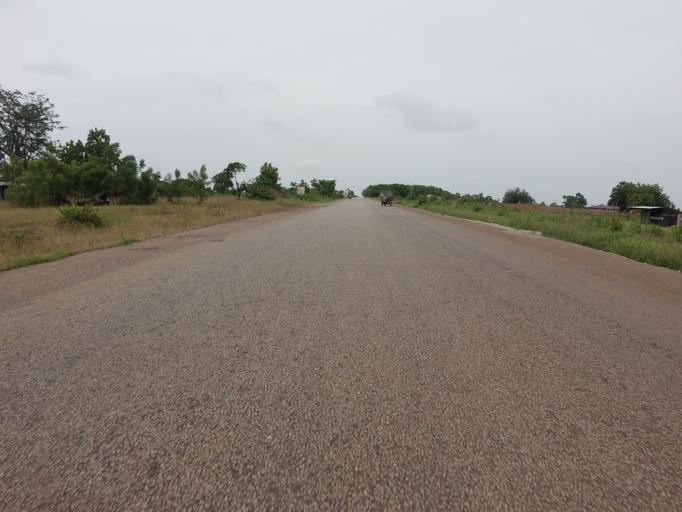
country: GH
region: Northern
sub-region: Yendi
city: Yendi
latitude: 9.4283
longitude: -0.0086
